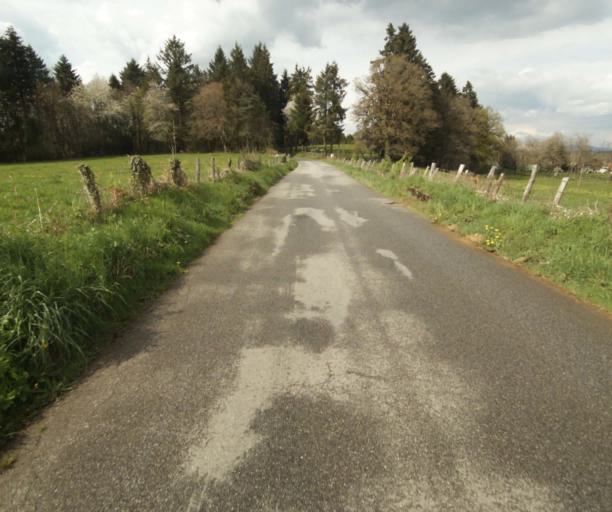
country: FR
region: Limousin
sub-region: Departement de la Correze
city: Tulle
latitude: 45.2854
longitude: 1.7449
